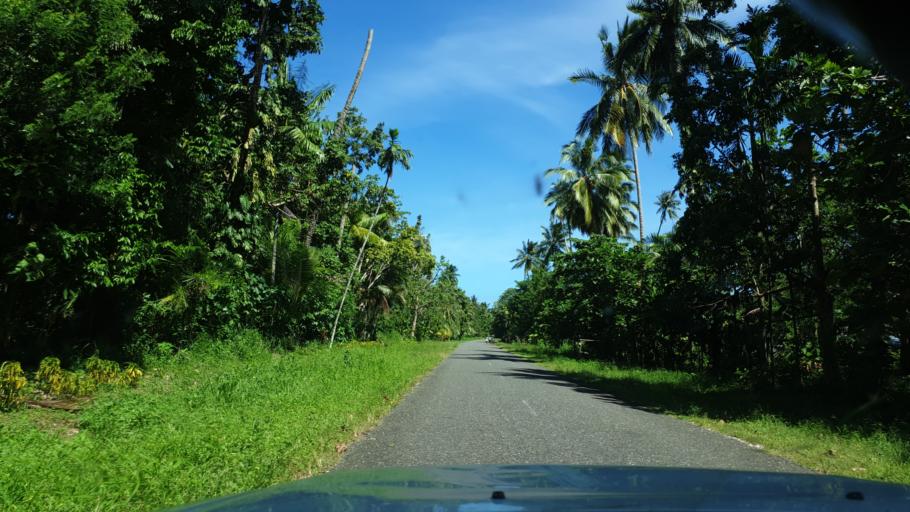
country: PG
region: Madang
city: Madang
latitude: -4.4826
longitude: 145.4220
